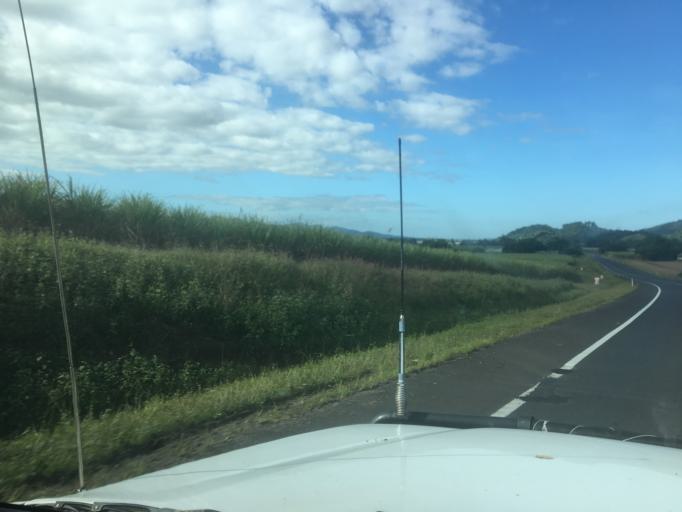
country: AU
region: Queensland
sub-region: Cassowary Coast
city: Innisfail
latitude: -17.2667
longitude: 145.9194
